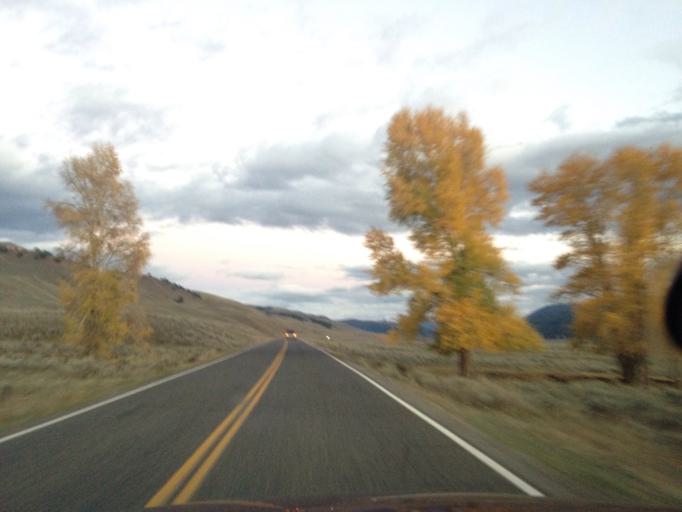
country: US
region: Montana
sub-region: Park County
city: Livingston
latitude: 44.8938
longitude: -110.2344
